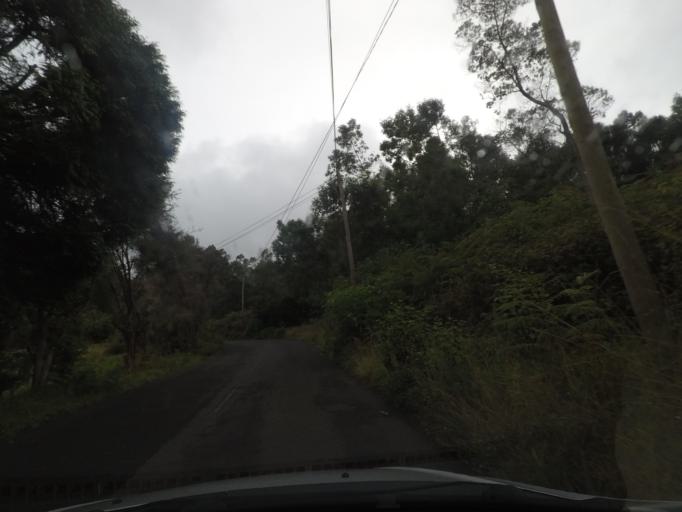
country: PT
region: Madeira
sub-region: Santana
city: Santana
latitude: 32.7915
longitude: -16.8863
